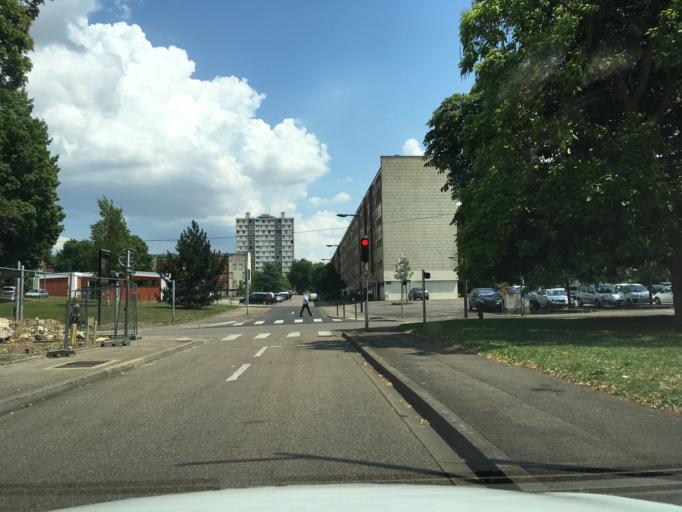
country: FR
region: Lorraine
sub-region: Departement de la Moselle
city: Saint-Julien-les-Metz
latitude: 49.1219
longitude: 6.1942
